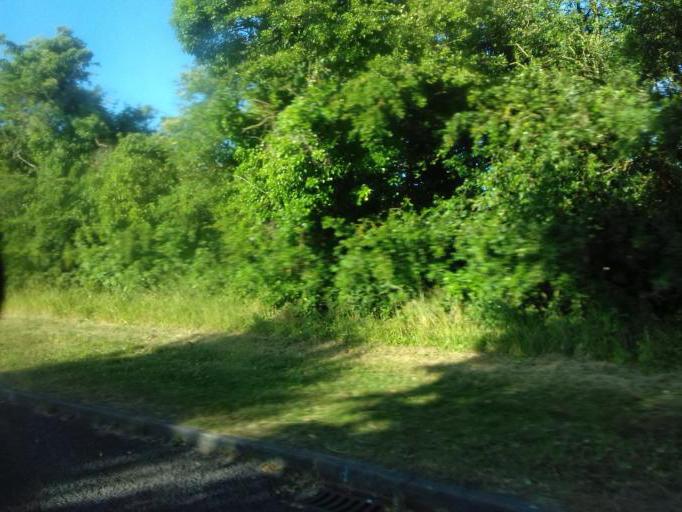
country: IE
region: Leinster
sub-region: Fingal County
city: Swords
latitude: 53.4914
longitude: -6.2986
